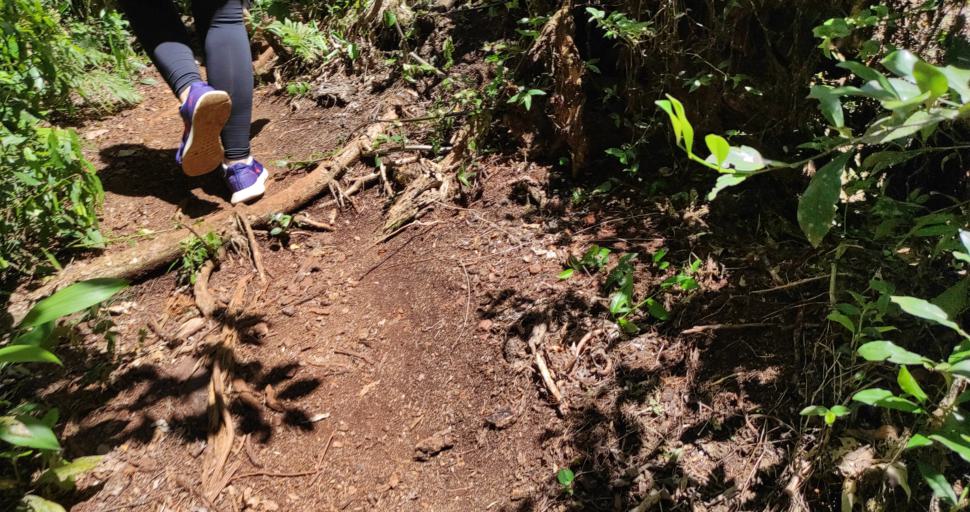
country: BR
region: Rio Grande do Sul
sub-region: Tres Passos
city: Tres Passos
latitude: -27.1484
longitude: -53.8977
